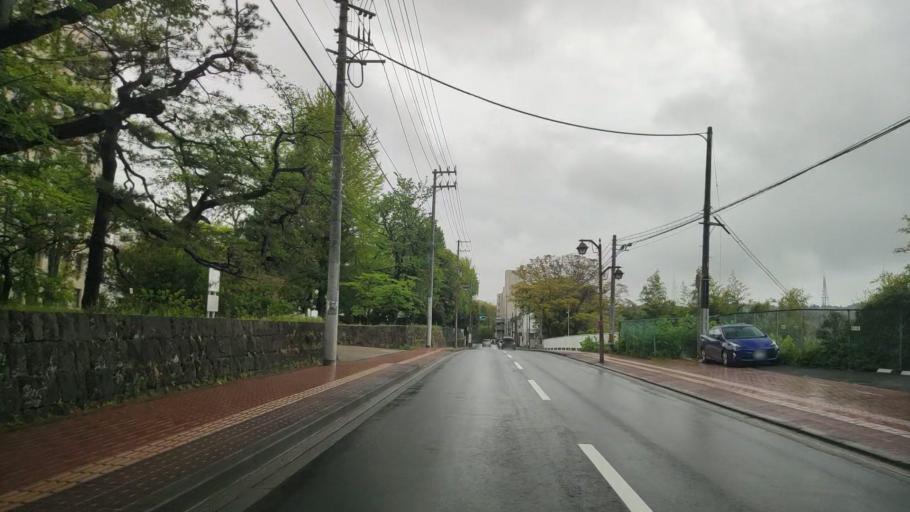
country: JP
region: Miyagi
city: Sendai
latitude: 38.2568
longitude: 140.8677
